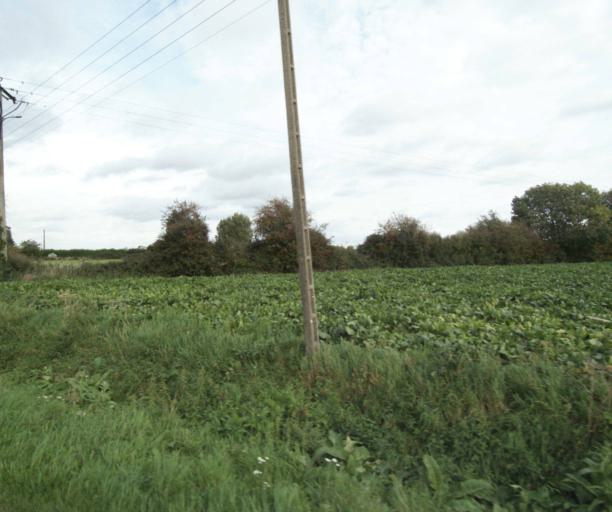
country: FR
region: Nord-Pas-de-Calais
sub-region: Departement du Nord
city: Bois-Grenier
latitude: 50.6611
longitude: 2.8837
